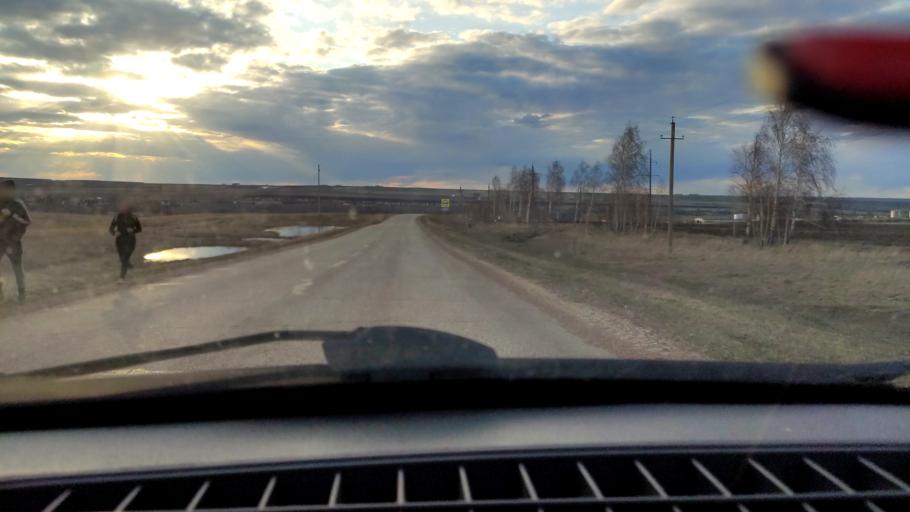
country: RU
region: Bashkortostan
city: Tolbazy
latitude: 54.0134
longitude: 55.7310
